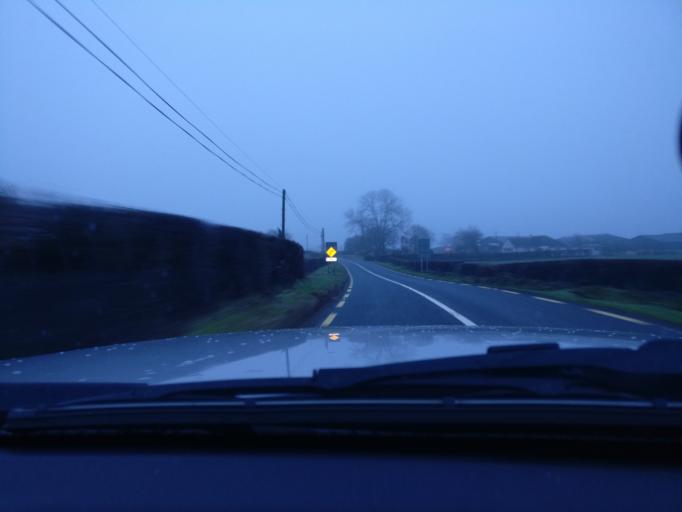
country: IE
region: Leinster
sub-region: An Mhi
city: Ballivor
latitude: 53.6115
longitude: -7.0532
